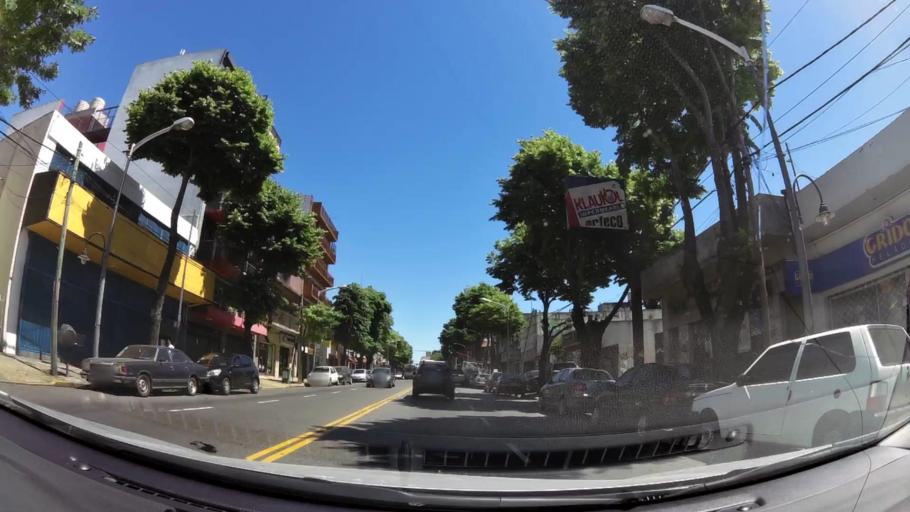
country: AR
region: Buenos Aires
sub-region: Partido de San Isidro
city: San Isidro
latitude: -34.4550
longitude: -58.5368
